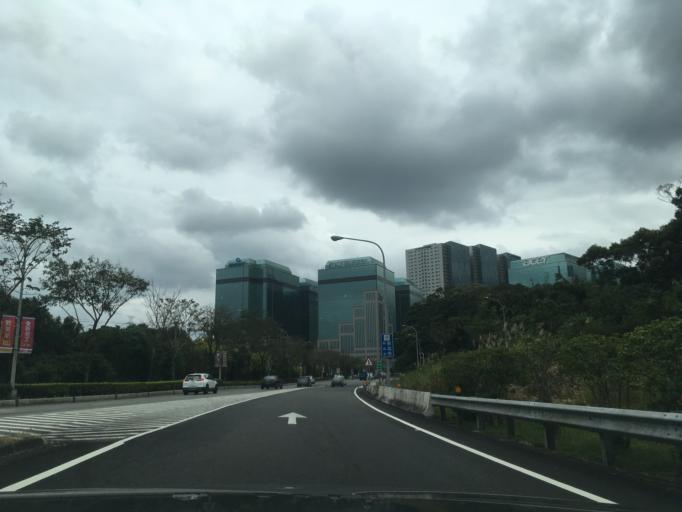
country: TW
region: Taipei
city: Taipei
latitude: 25.0578
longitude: 121.6424
